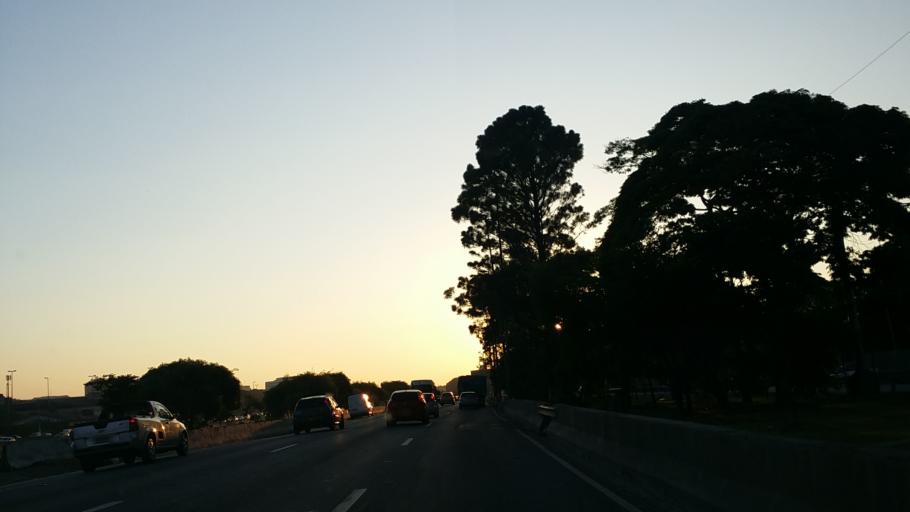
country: BR
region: Sao Paulo
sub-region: Sao Paulo
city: Sao Paulo
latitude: -23.5190
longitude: -46.6375
